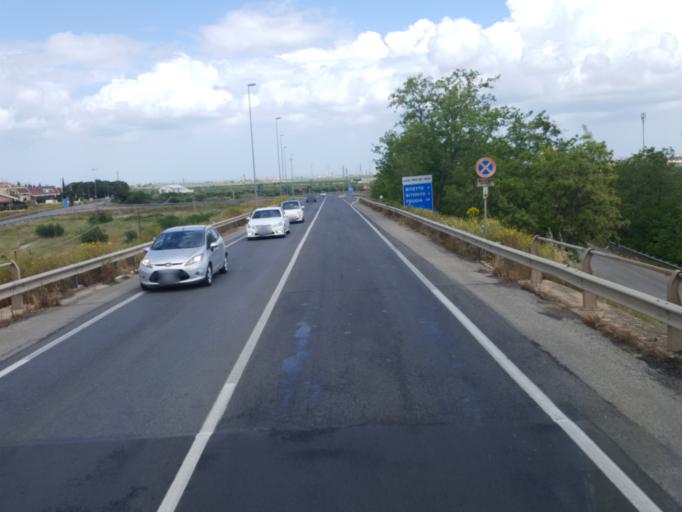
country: IT
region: Apulia
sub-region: Provincia di Bari
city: Palo del Colle
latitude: 41.0543
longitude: 16.7110
